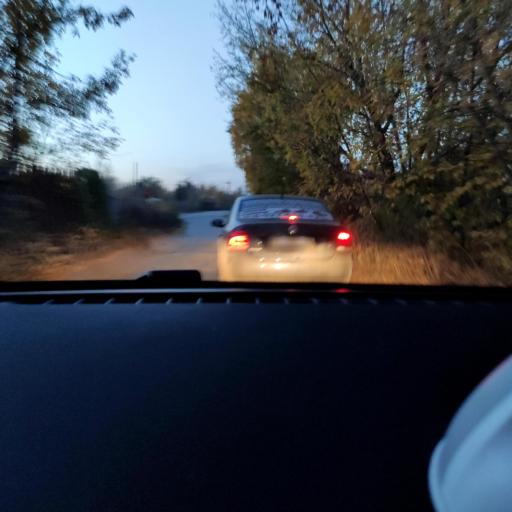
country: RU
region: Samara
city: Petra-Dubrava
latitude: 53.2963
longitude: 50.3046
